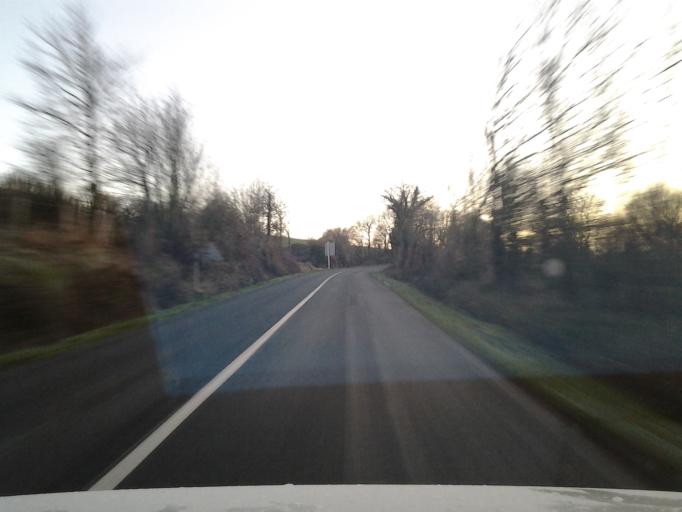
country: FR
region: Pays de la Loire
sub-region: Departement de la Vendee
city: Les Epesses
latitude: 46.8769
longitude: -0.9250
